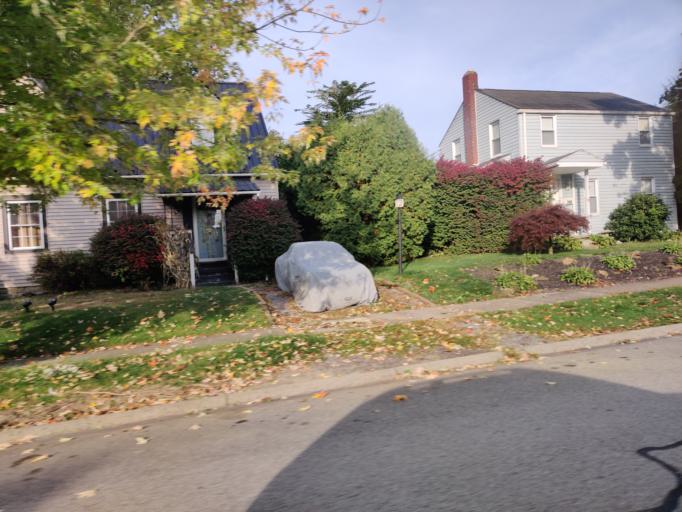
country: US
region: Pennsylvania
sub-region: Allegheny County
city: Brackenridge
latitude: 40.6283
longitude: -79.7254
